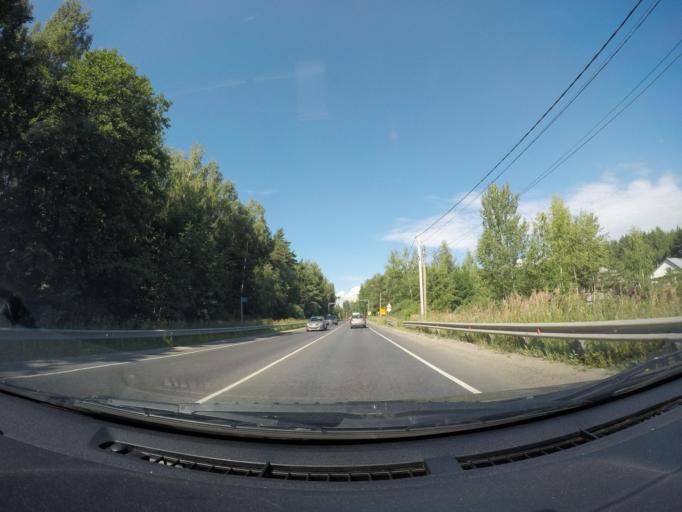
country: RU
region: Moskovskaya
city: Ramenskoye
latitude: 55.6367
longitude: 38.2958
